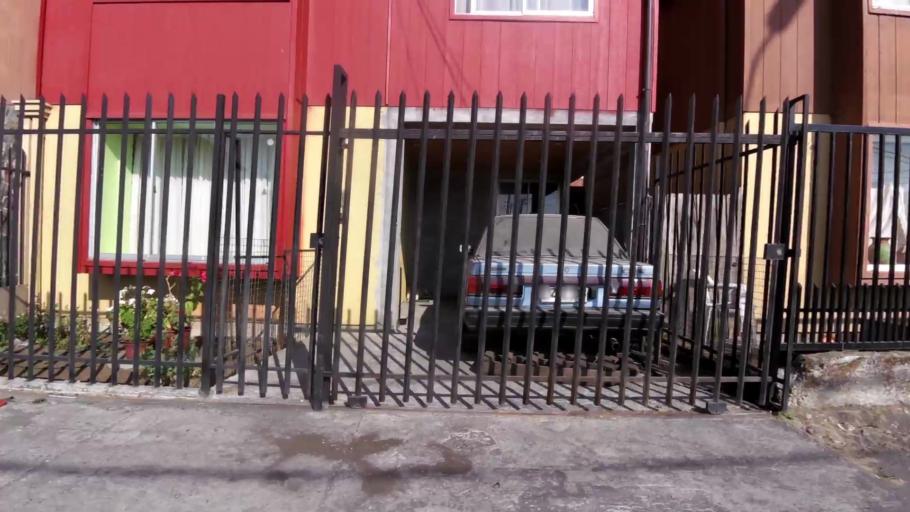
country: CL
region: Biobio
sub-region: Provincia de Concepcion
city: Talcahuano
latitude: -36.7920
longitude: -73.1152
